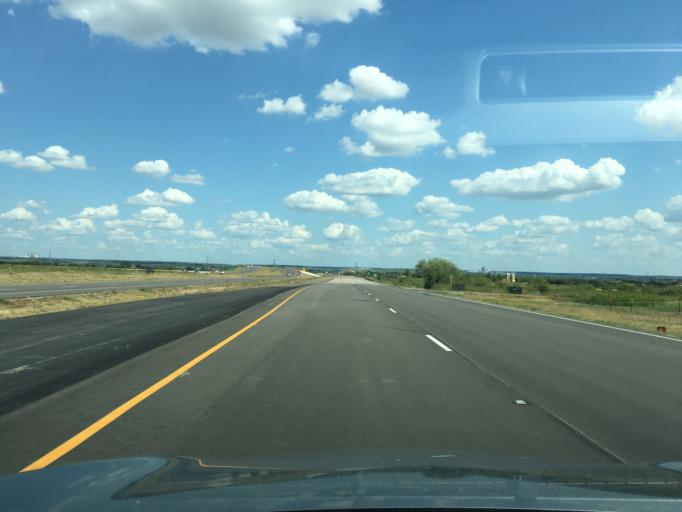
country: US
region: Texas
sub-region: Tarrant County
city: Mansfield
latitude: 32.5257
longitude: -97.0895
